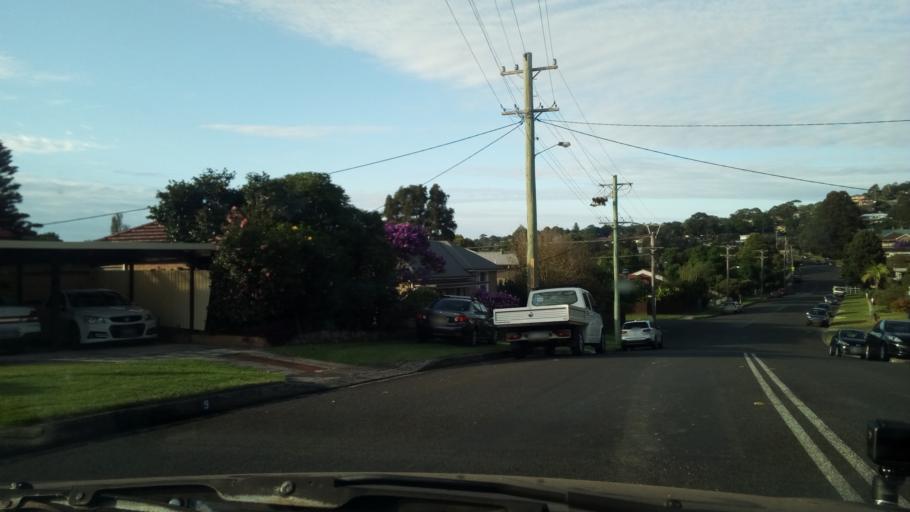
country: AU
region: New South Wales
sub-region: Wollongong
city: Mount Ousley
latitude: -34.3838
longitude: 150.8736
